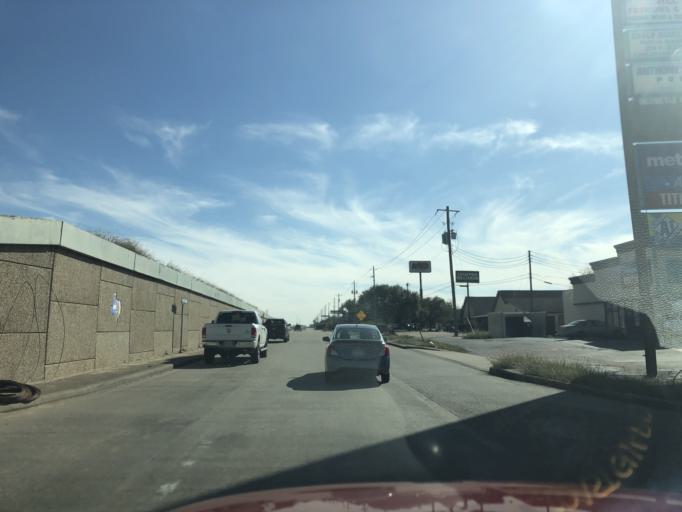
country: US
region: Texas
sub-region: Galveston County
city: League City
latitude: 29.5027
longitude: -95.1144
